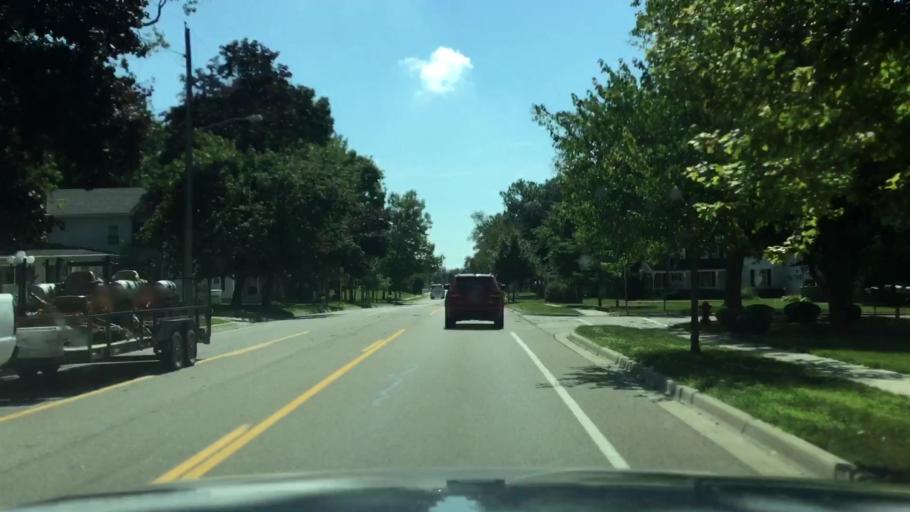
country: US
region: Michigan
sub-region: Lenawee County
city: Clinton
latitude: 42.0693
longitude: -83.9699
